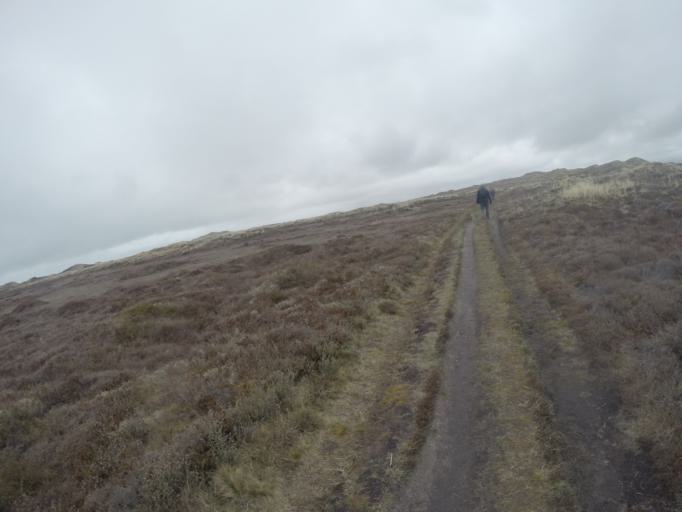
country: DK
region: Central Jutland
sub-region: Lemvig Kommune
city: Thyboron
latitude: 56.8317
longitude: 8.2675
